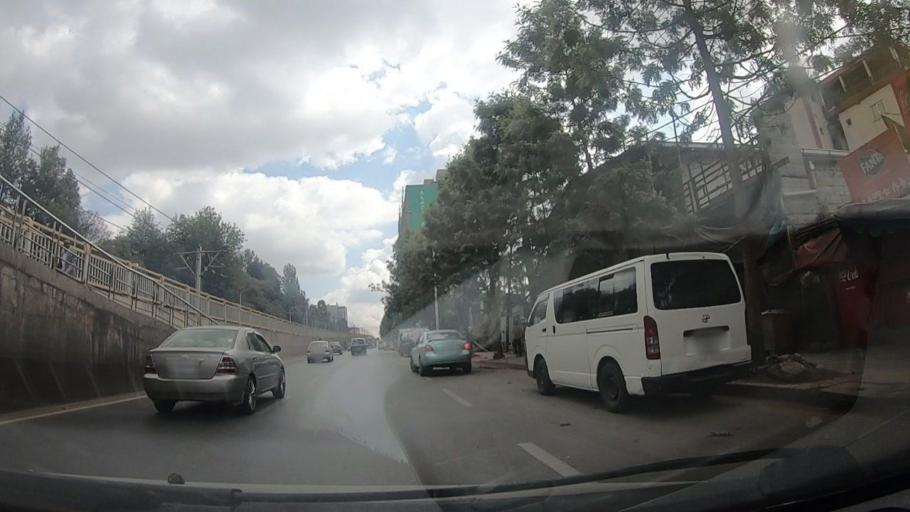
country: ET
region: Adis Abeba
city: Addis Ababa
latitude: 9.0118
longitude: 38.7295
